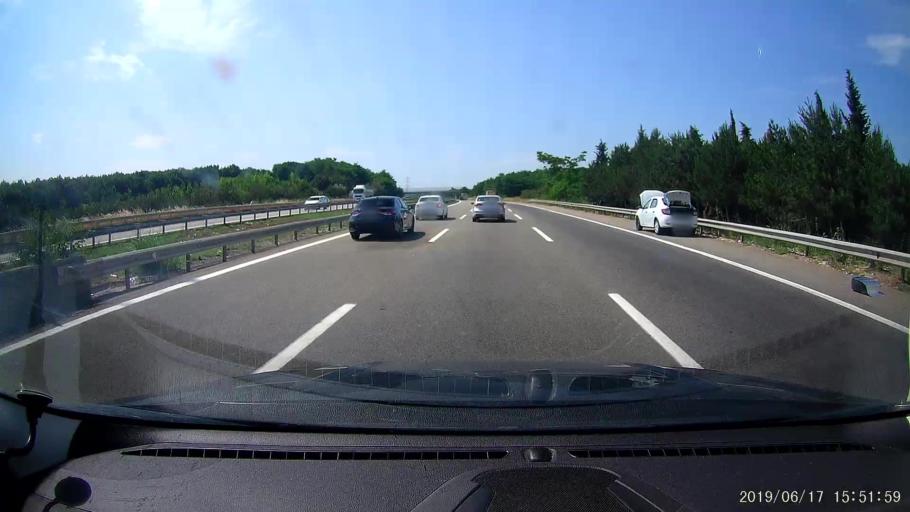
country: TR
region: Istanbul
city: Canta
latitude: 41.1823
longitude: 28.1121
